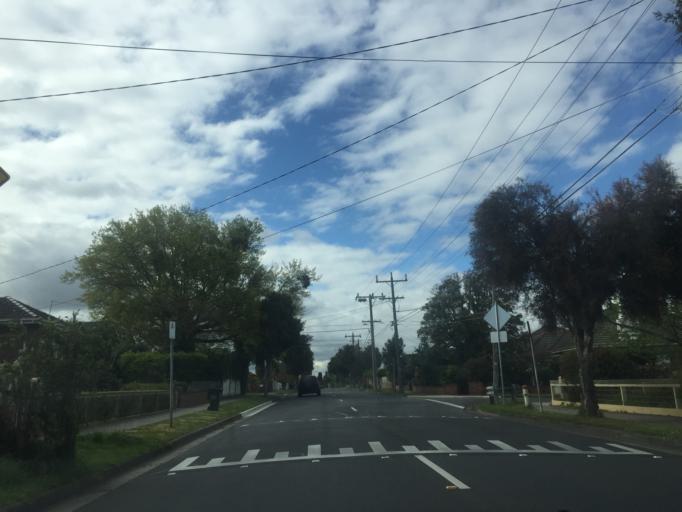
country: AU
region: Victoria
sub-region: Darebin
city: Reservoir
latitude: -37.7275
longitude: 145.0143
